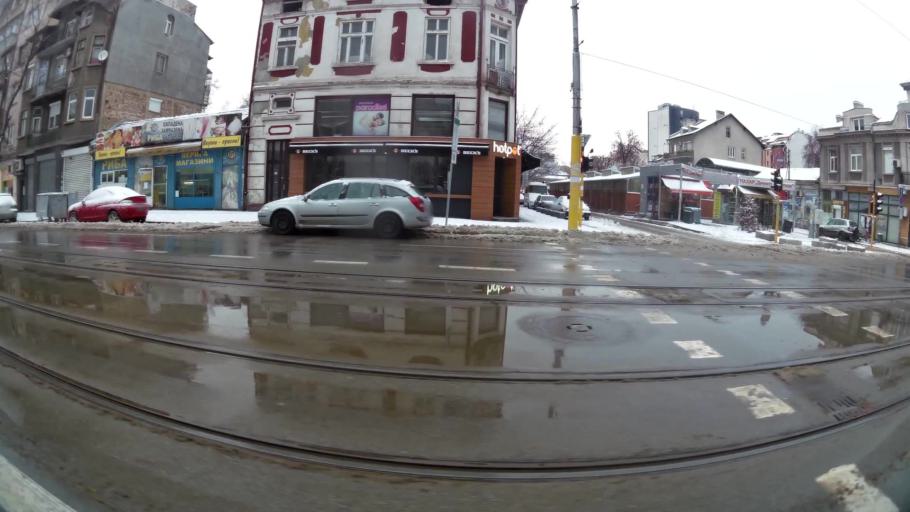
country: BG
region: Sofia-Capital
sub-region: Stolichna Obshtina
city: Sofia
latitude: 42.7000
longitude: 23.3001
